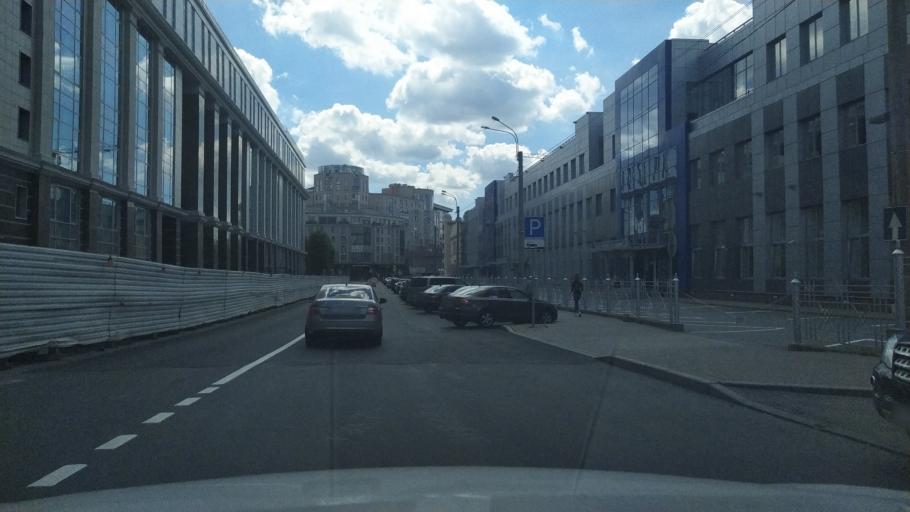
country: RU
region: St.-Petersburg
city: Novaya Derevnya
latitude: 59.9684
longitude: 30.2885
